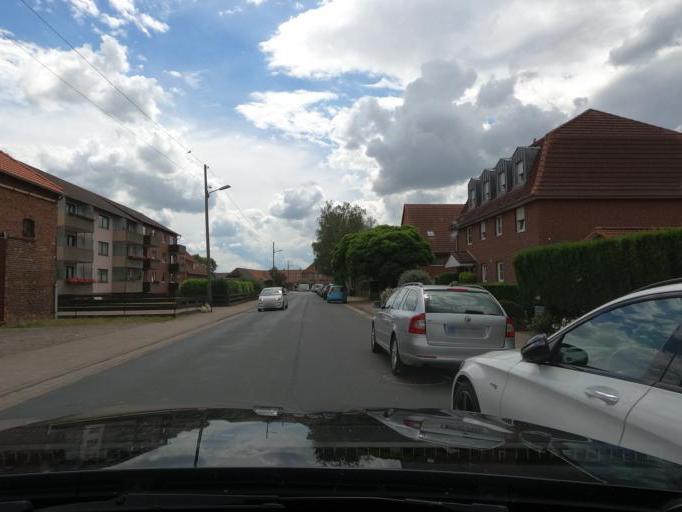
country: DE
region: Lower Saxony
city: Sehnde
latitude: 52.3406
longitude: 9.9113
